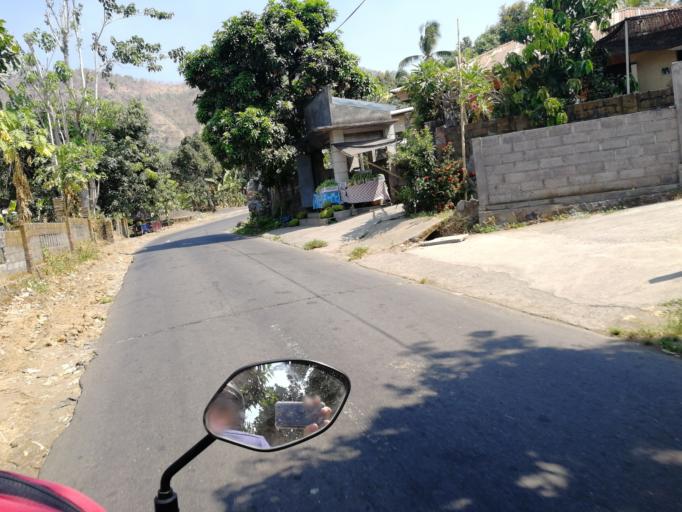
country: ID
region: Bali
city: Banjar Trunyan
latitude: -8.1251
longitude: 115.3289
